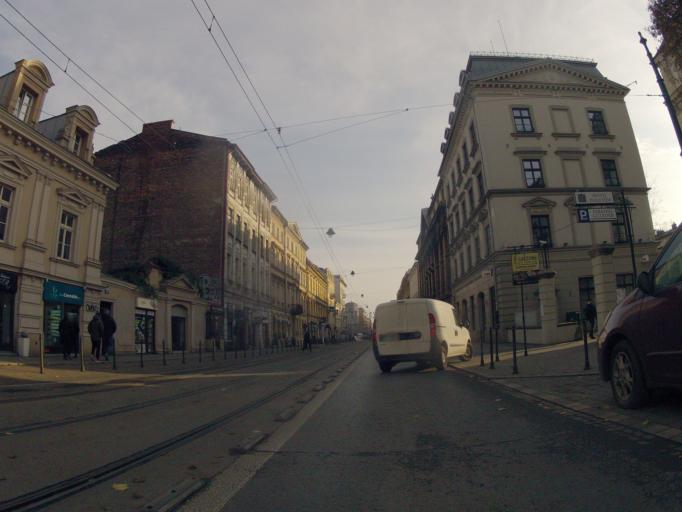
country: PL
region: Lesser Poland Voivodeship
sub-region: Krakow
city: Krakow
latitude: 50.0582
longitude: 19.9437
